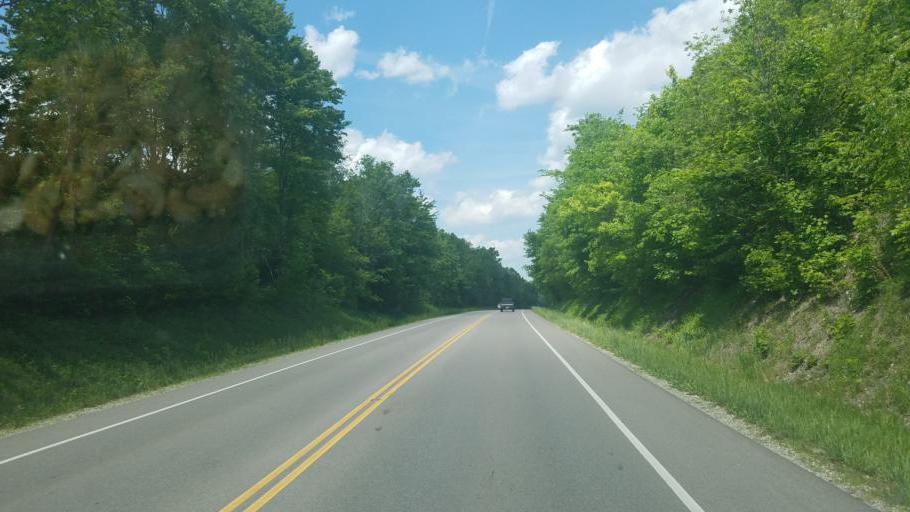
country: US
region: Ohio
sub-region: Meigs County
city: Middleport
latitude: 39.0141
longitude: -82.0681
